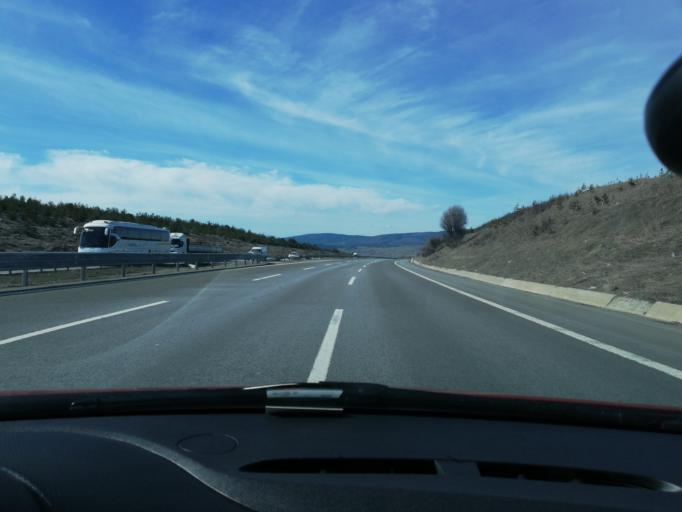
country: TR
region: Bolu
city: Yenicaga
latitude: 40.7574
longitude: 32.0651
